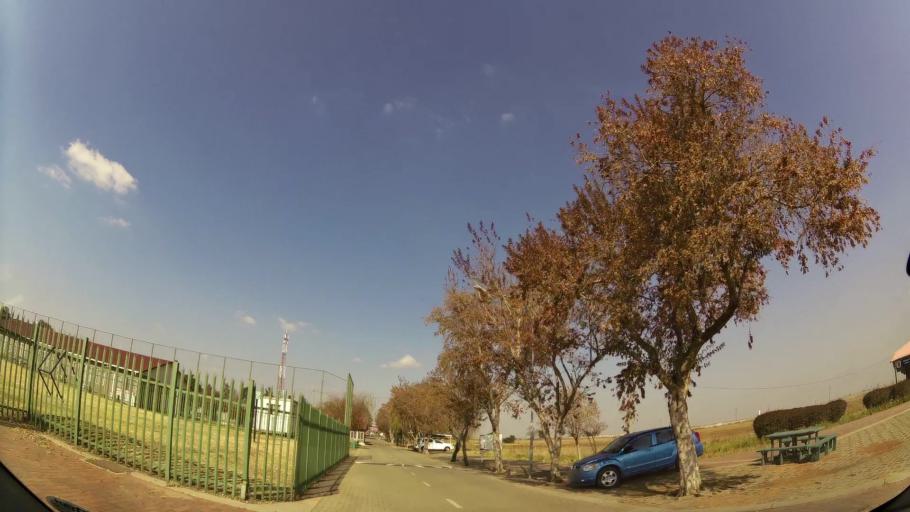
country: ZA
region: Gauteng
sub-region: Ekurhuleni Metropolitan Municipality
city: Benoni
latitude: -26.1423
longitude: 28.3971
